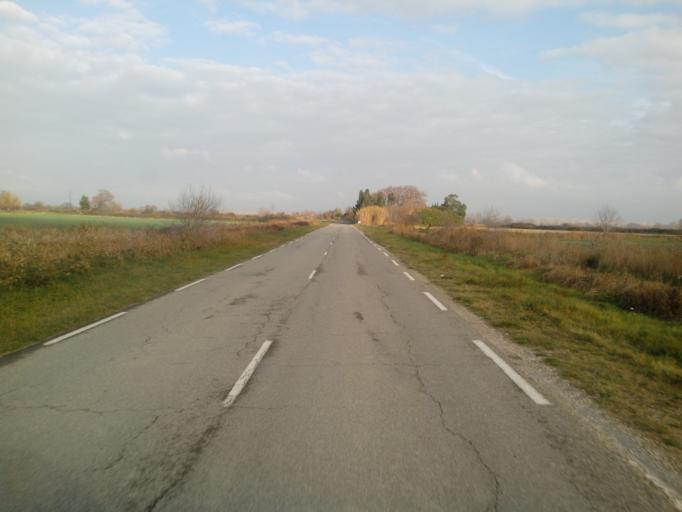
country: FR
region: Provence-Alpes-Cote d'Azur
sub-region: Departement des Bouches-du-Rhone
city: Arles
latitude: 43.5747
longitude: 4.6310
